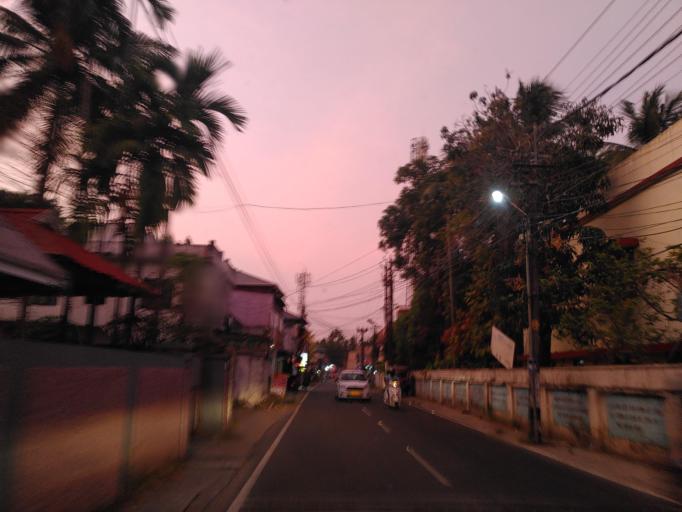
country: IN
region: Kerala
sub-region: Ernakulam
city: Cochin
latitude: 9.9124
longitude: 76.2792
